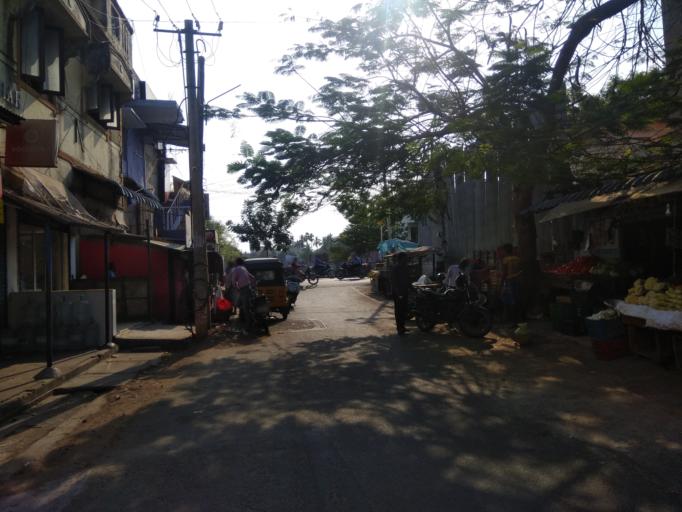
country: IN
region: Tamil Nadu
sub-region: Kancheepuram
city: Saint Thomas Mount
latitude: 12.9841
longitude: 80.1888
